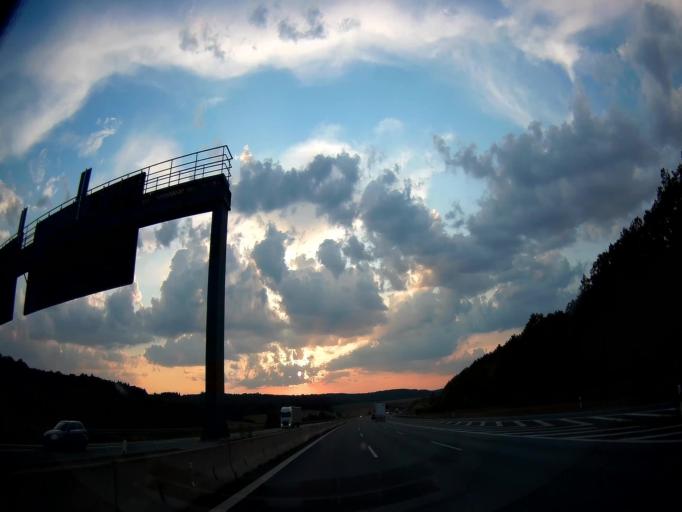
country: DE
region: Bavaria
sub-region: Regierungsbezirk Unterfranken
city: Waldbrunn
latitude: 49.7488
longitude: 9.8041
